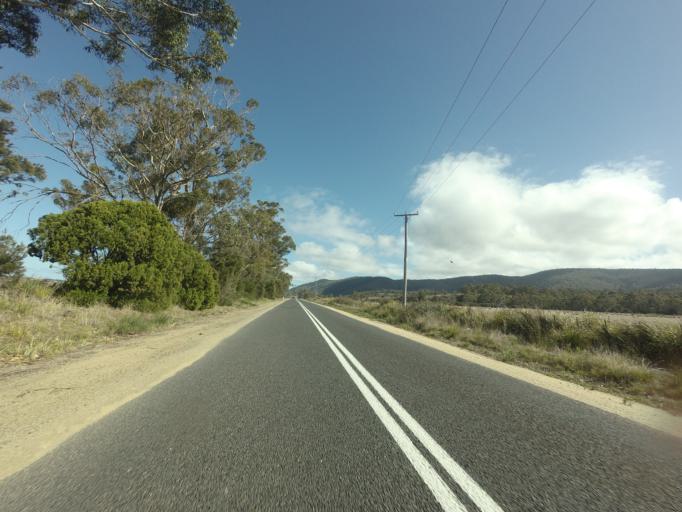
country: AU
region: Tasmania
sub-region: Break O'Day
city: St Helens
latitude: -41.7007
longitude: 148.2756
